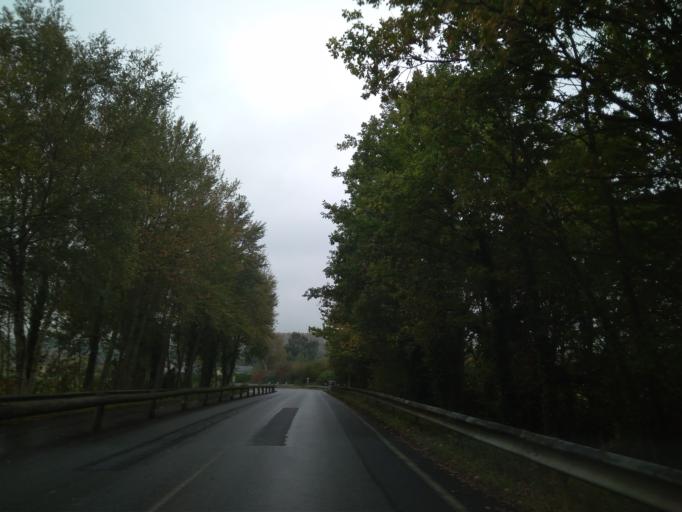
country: FR
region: Brittany
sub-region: Departement d'Ille-et-Vilaine
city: Saint-Gregoire
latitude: 48.1481
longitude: -1.6707
